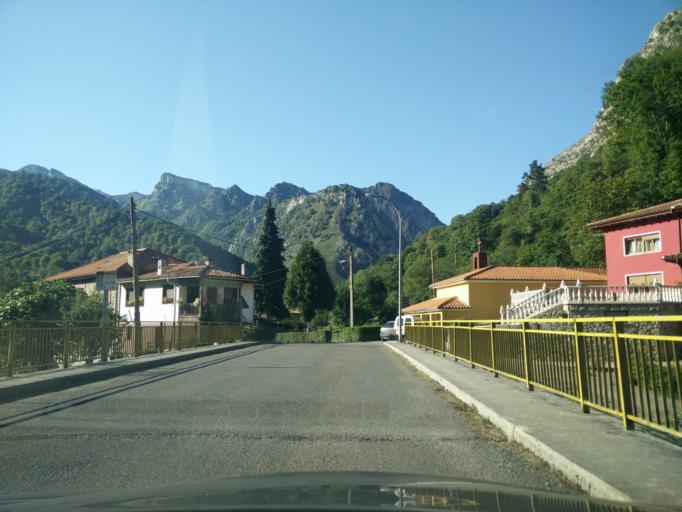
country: ES
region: Asturias
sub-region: Province of Asturias
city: Parres
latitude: 43.2573
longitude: -5.2015
